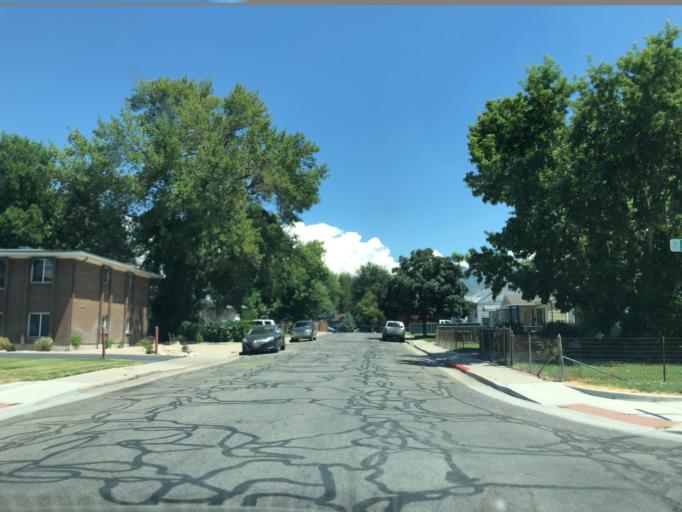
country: US
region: Utah
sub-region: Salt Lake County
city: South Salt Lake
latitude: 40.7210
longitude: -111.8756
